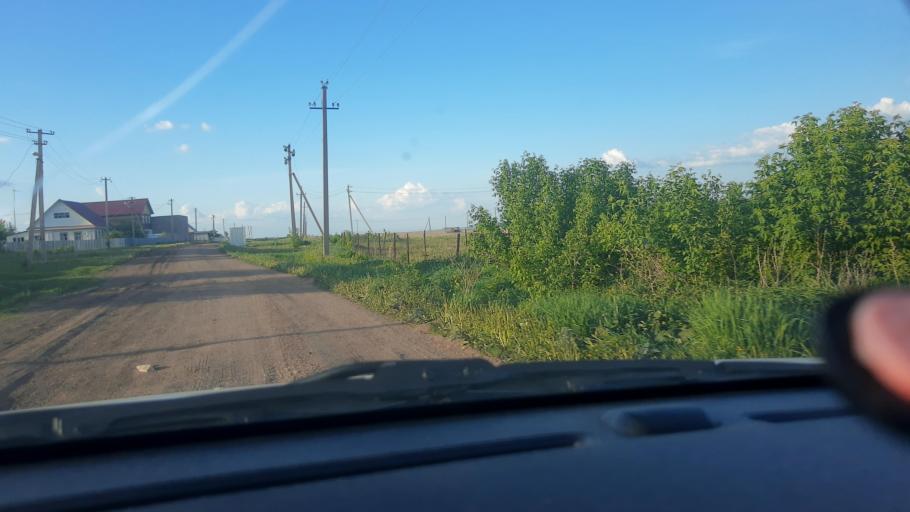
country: RU
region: Bashkortostan
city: Karmaskaly
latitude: 54.3827
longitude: 55.9397
